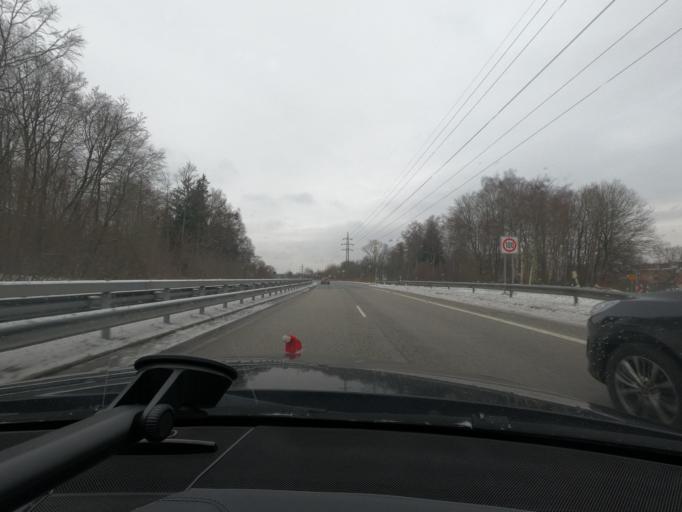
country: DE
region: Schleswig-Holstein
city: Harrislee
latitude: 54.7947
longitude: 9.4093
